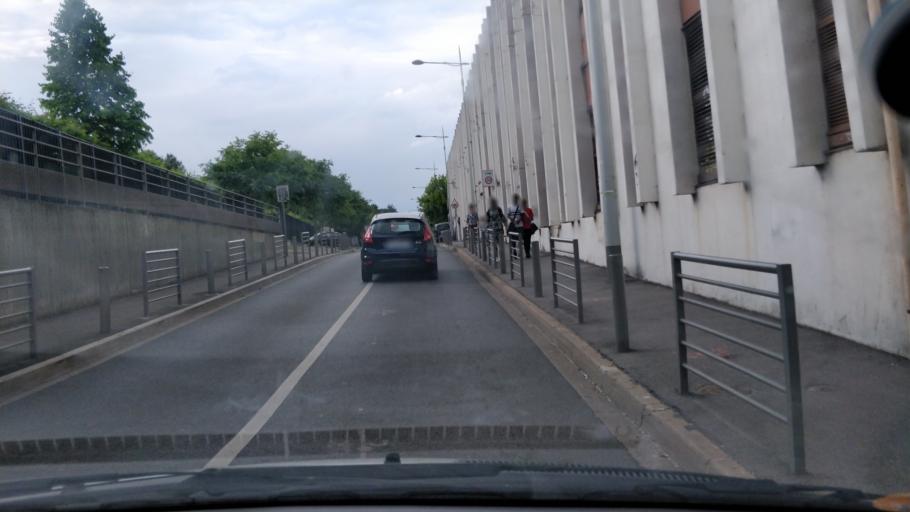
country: FR
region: Ile-de-France
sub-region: Departement de Seine-Saint-Denis
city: Bagnolet
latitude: 48.8639
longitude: 2.4259
